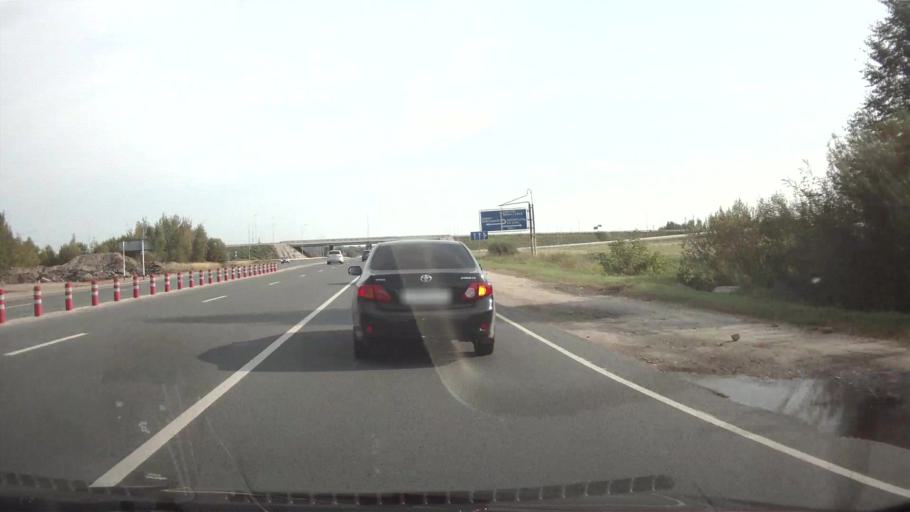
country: RU
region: Mariy-El
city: Yoshkar-Ola
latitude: 56.6775
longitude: 48.0185
